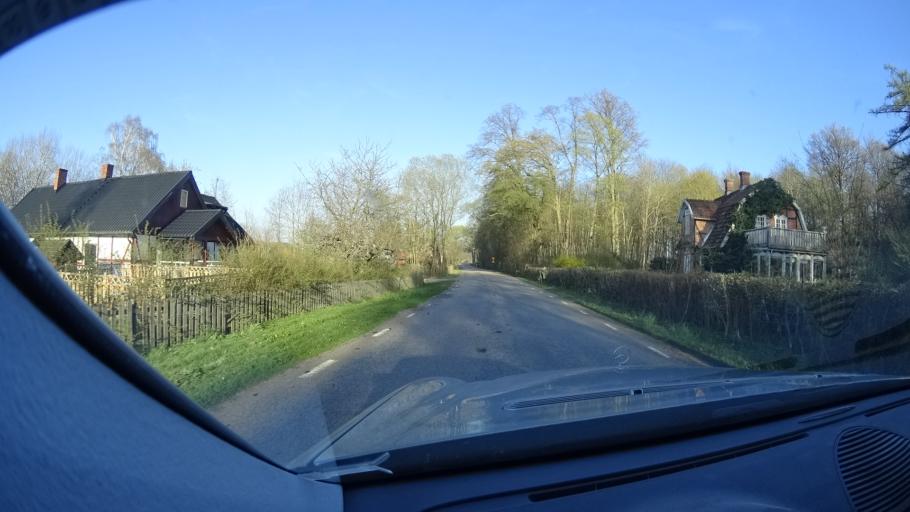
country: SE
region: Skane
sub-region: Hoors Kommun
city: Satofta
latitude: 55.8656
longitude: 13.4928
